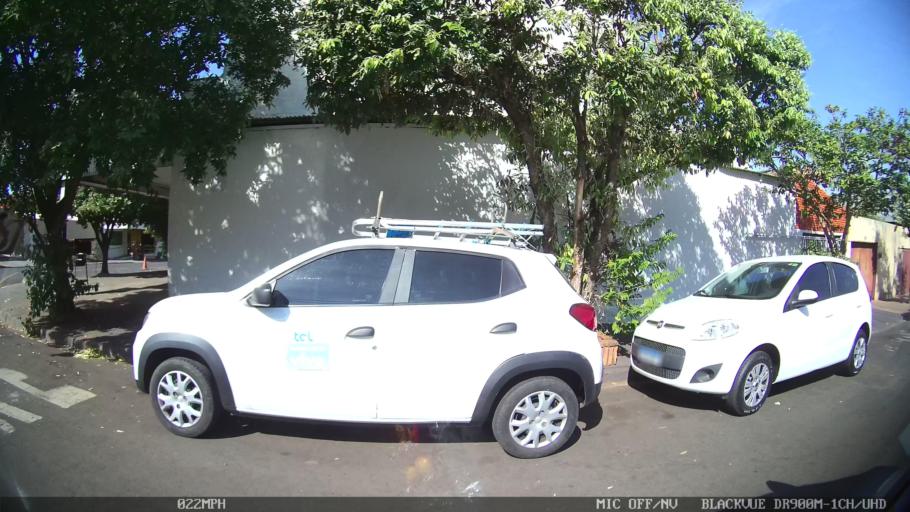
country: BR
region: Sao Paulo
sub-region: Sao Jose Do Rio Preto
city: Sao Jose do Rio Preto
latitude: -20.7859
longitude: -49.4085
